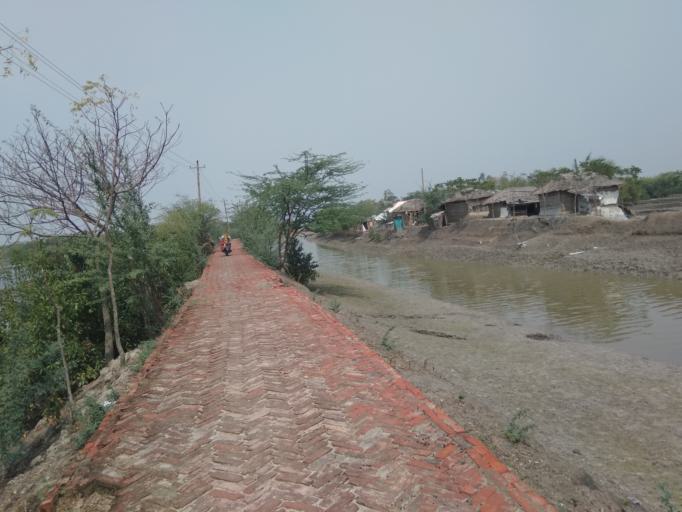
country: IN
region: West Bengal
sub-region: North 24 Parganas
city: Taki
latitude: 22.2790
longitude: 89.2845
